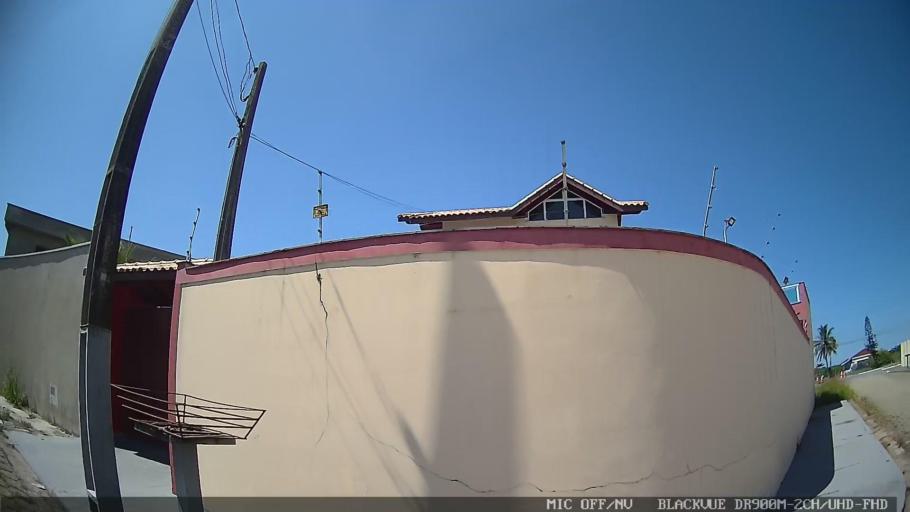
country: BR
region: Sao Paulo
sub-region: Peruibe
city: Peruibe
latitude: -24.3284
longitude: -47.0014
